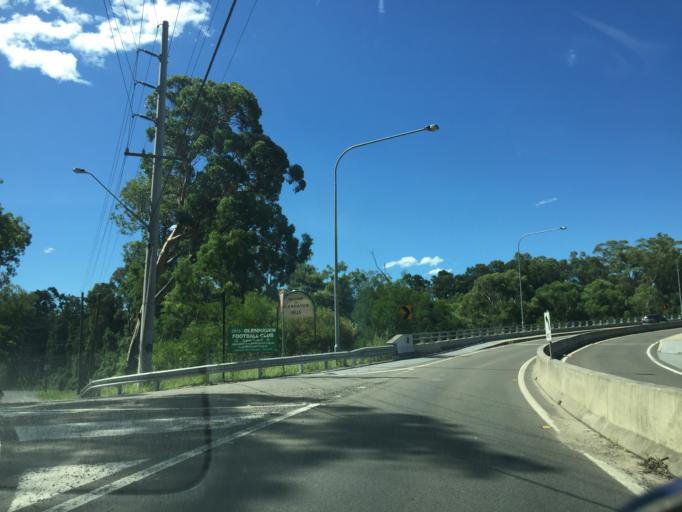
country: AU
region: New South Wales
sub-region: The Hills Shire
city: Beaumont Hills
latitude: -33.6946
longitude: 150.9696
